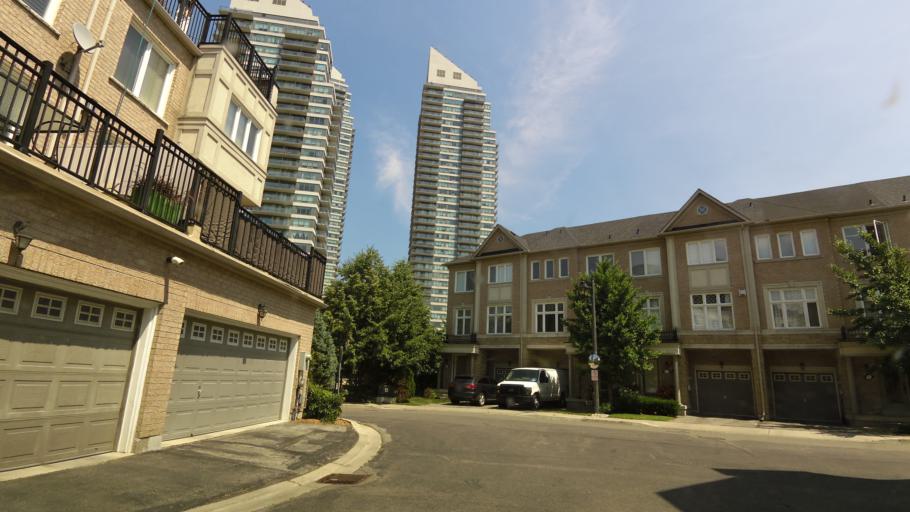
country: CA
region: Ontario
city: Etobicoke
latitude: 43.6212
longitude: -79.4854
